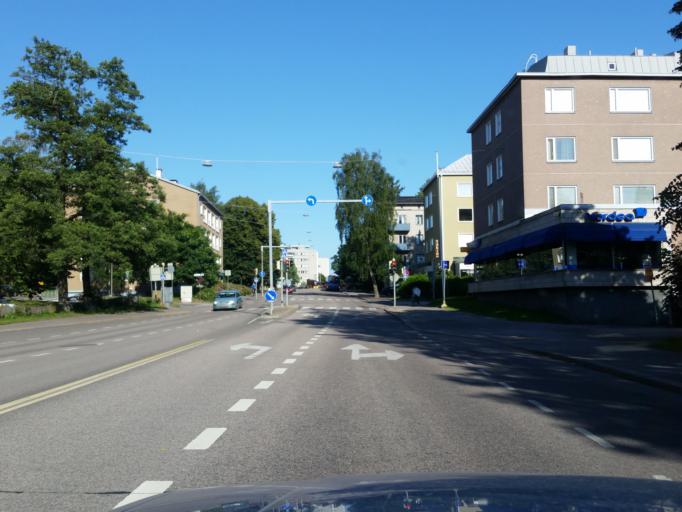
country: FI
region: Uusimaa
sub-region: Helsinki
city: Teekkarikylae
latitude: 60.1608
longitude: 24.8765
